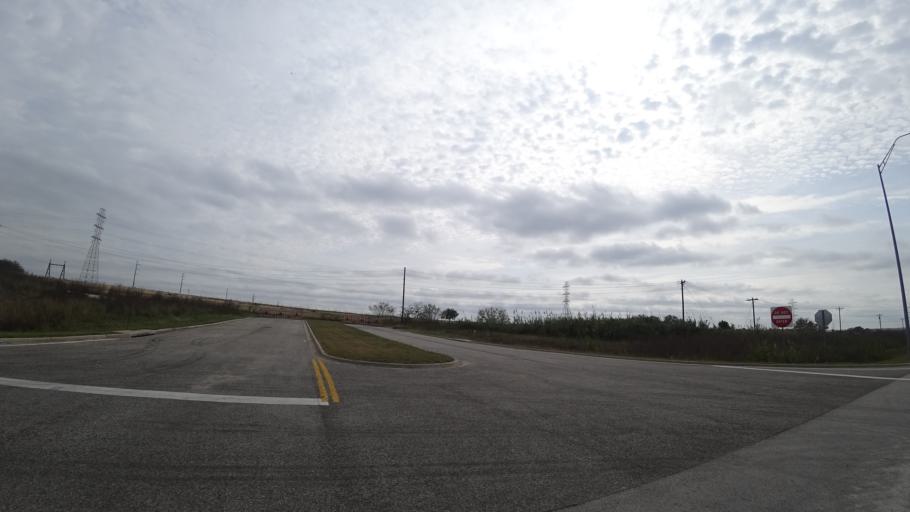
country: US
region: Texas
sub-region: Travis County
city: Manor
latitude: 30.3696
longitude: -97.5826
